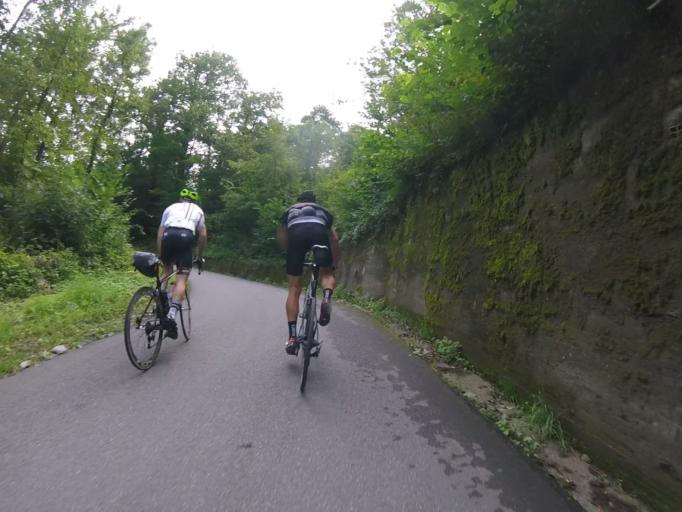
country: IT
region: Lombardy
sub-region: Provincia di Sondrio
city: Mazzo di Valtellina
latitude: 46.2509
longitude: 10.2579
